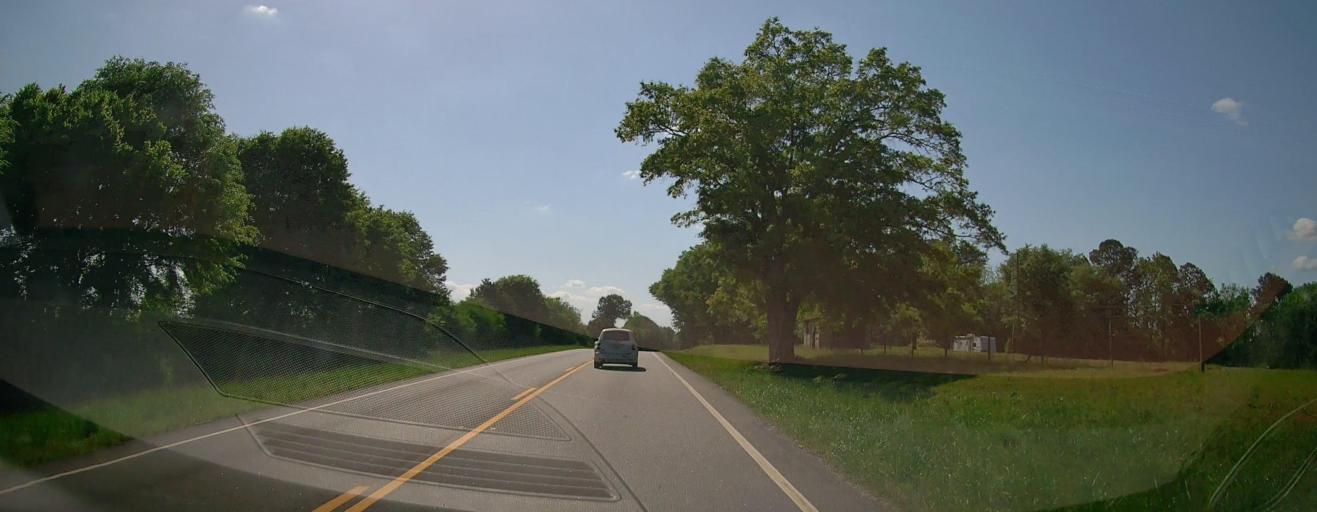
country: US
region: Georgia
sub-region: Morgan County
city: Madison
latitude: 33.5984
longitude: -83.4088
